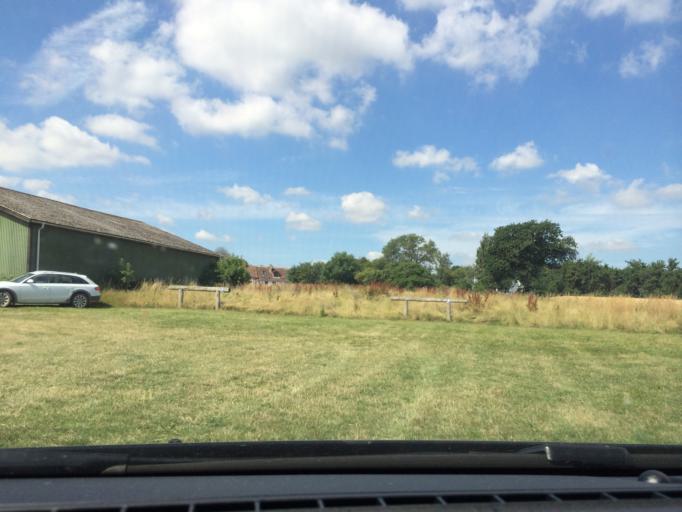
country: DK
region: Zealand
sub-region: Vordingborg Kommune
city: Stege
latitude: 55.0424
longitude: 12.1978
